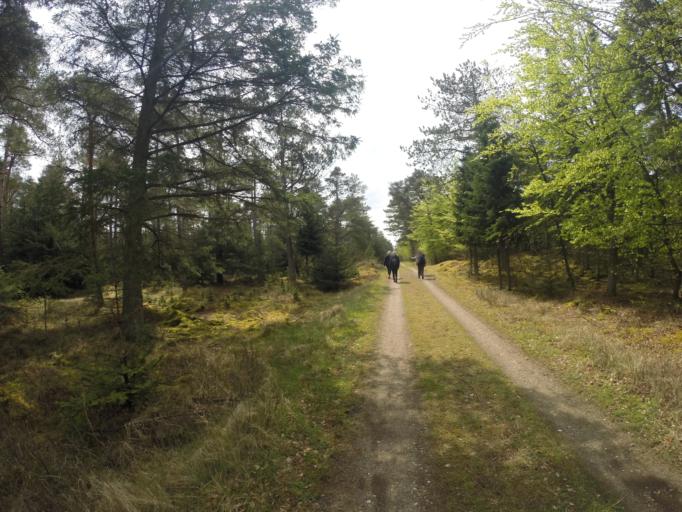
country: DK
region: North Denmark
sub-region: Thisted Kommune
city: Hanstholm
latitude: 57.0381
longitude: 8.5706
